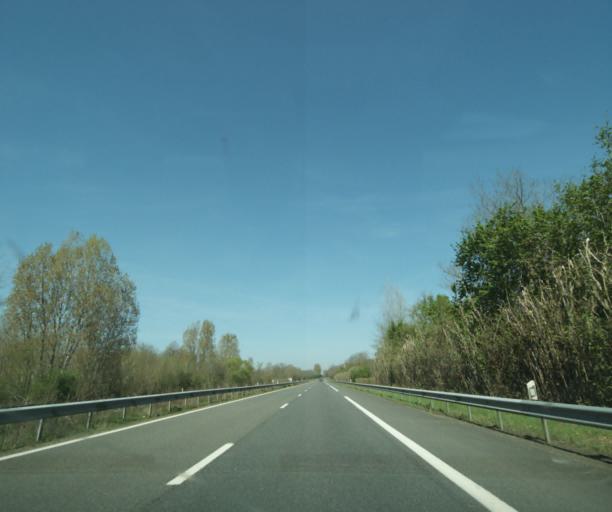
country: FR
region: Bourgogne
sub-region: Departement de la Nievre
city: La Charite-sur-Loire
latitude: 47.2219
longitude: 3.0039
